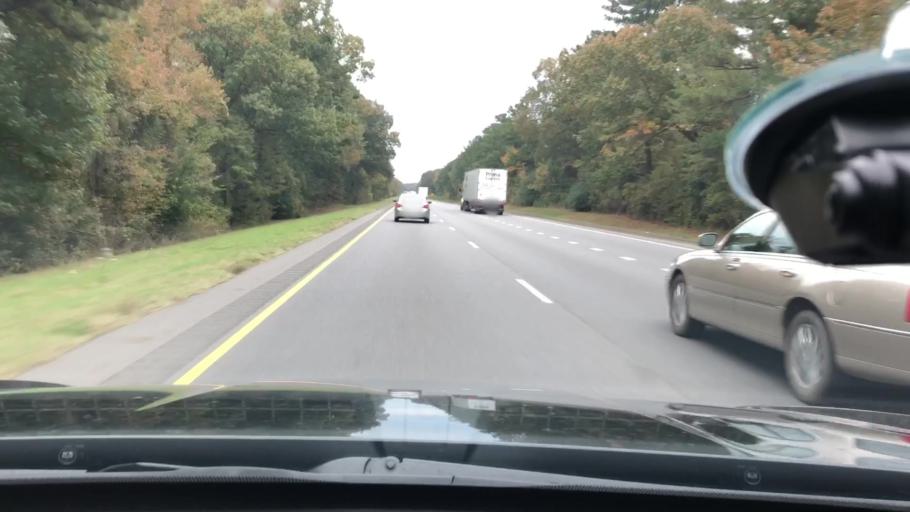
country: US
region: Arkansas
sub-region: Hempstead County
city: Hope
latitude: 33.6518
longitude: -93.6668
